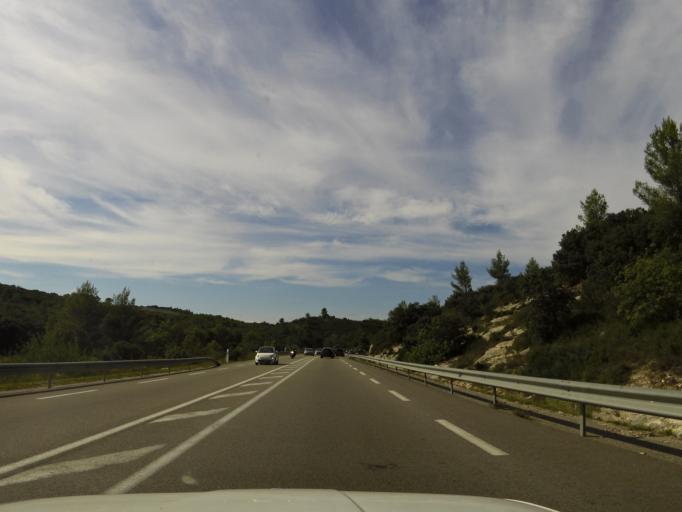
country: FR
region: Languedoc-Roussillon
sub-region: Departement du Gard
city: La Calmette
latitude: 43.8906
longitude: 4.2915
